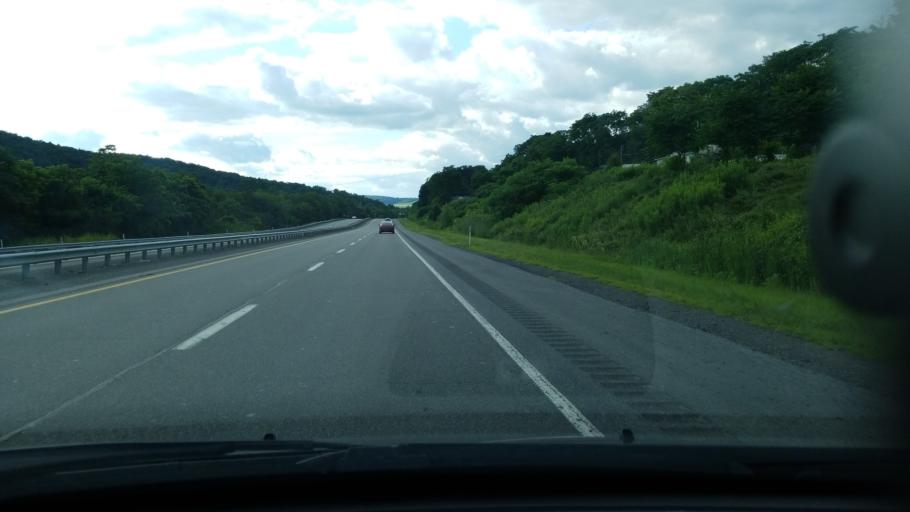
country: US
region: Pennsylvania
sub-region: Montour County
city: Danville
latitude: 40.9748
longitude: -76.6198
